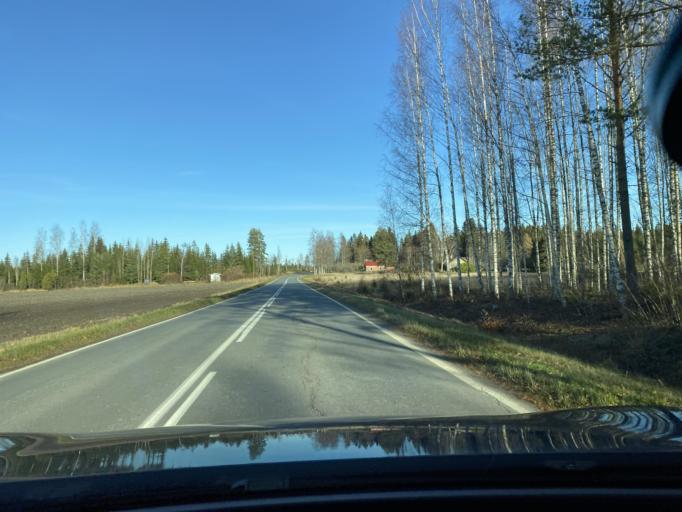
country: FI
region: Haeme
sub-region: Forssa
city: Tammela
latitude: 60.8483
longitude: 23.8392
